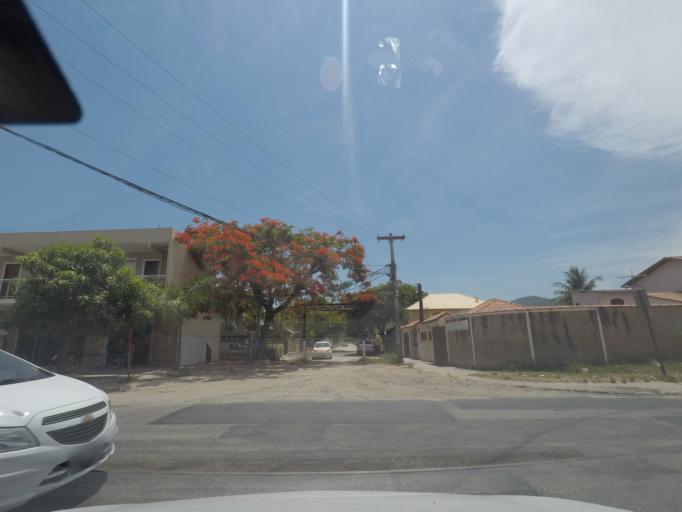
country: BR
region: Rio de Janeiro
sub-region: Marica
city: Marica
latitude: -22.9544
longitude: -42.9621
